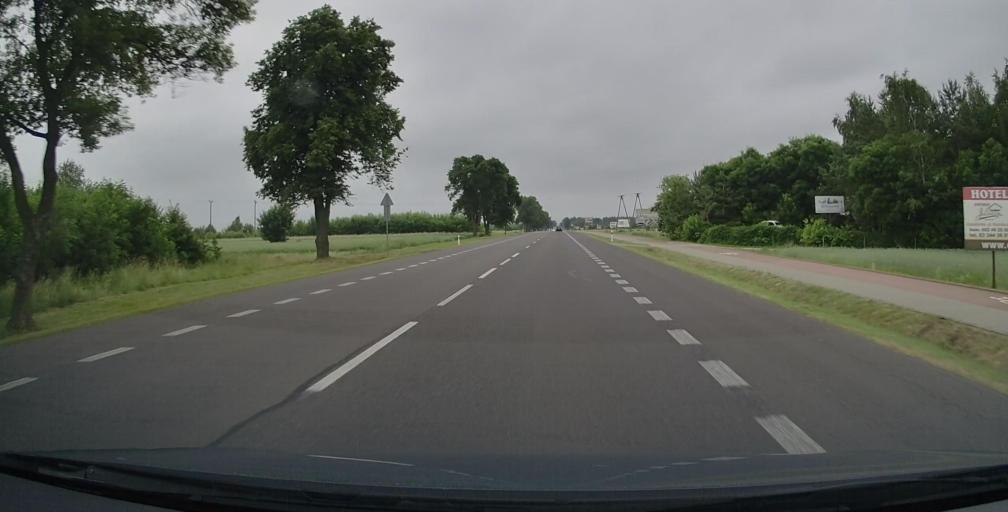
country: PL
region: Lublin Voivodeship
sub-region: Biala Podlaska
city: Biala Podlaska
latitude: 52.0342
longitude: 23.0506
